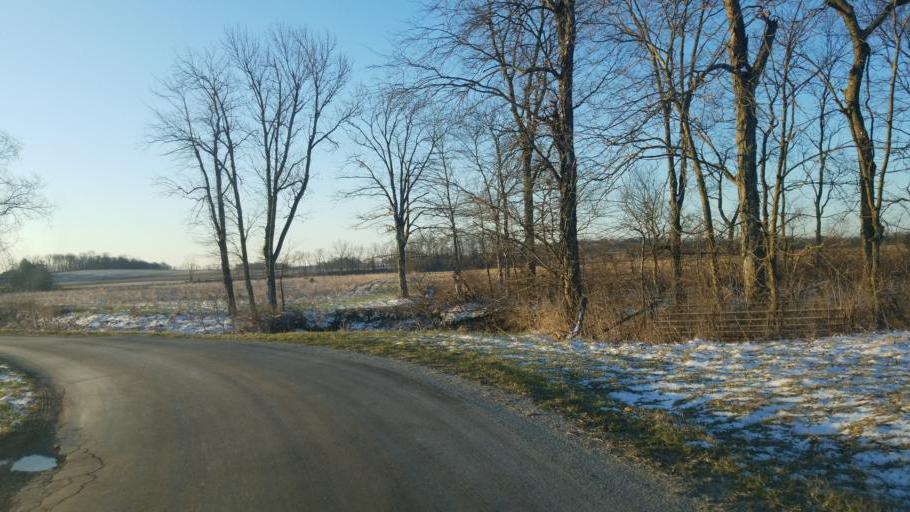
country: US
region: Ohio
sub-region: Highland County
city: Leesburg
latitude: 39.2576
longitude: -83.5161
